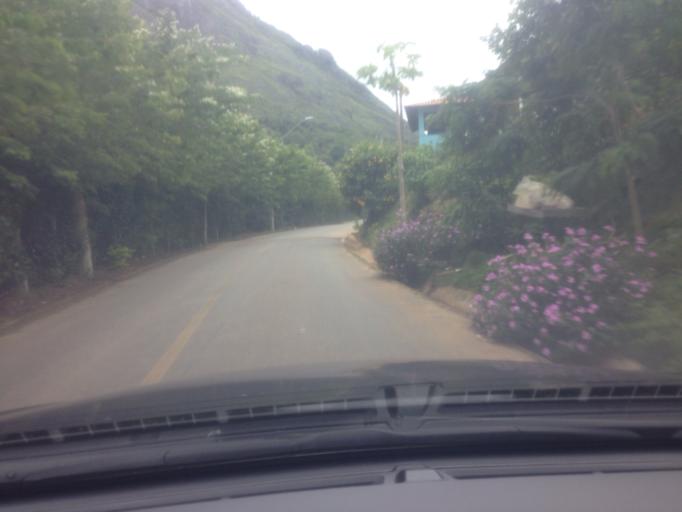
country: BR
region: Espirito Santo
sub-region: Guarapari
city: Guarapari
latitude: -20.5859
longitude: -40.5394
